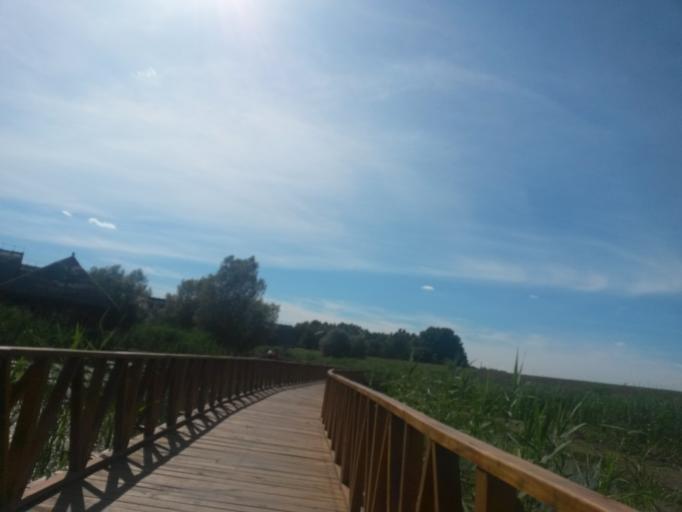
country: HR
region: Osjecko-Baranjska
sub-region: Grad Osijek
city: Bilje
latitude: 45.6081
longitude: 18.7907
